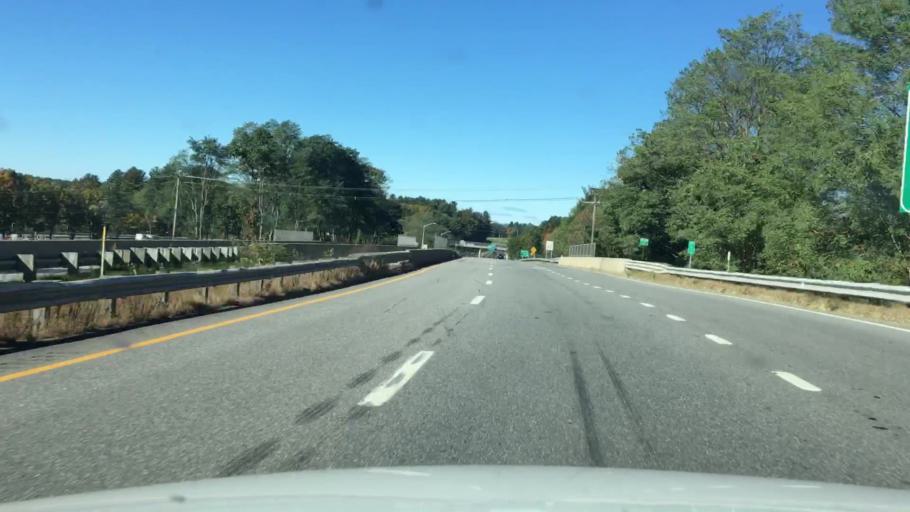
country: US
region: New Hampshire
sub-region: Strafford County
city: Dover
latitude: 43.1813
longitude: -70.8759
